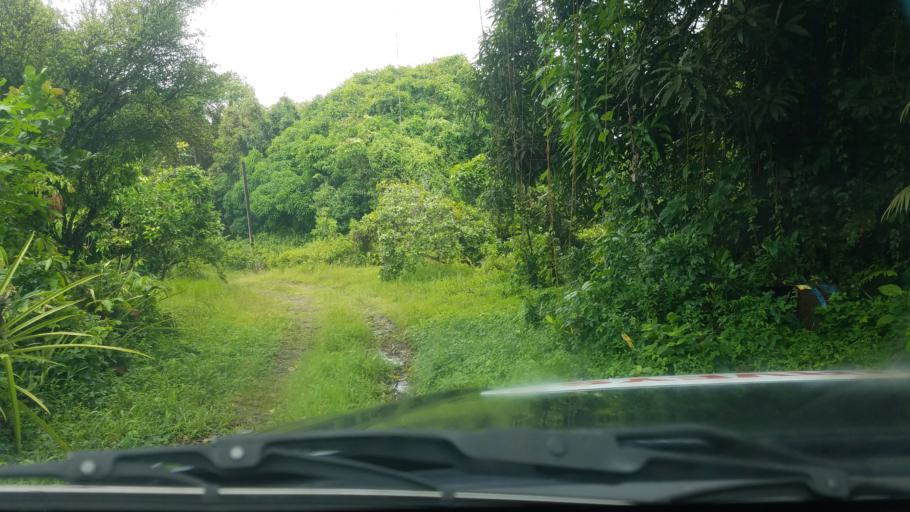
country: LC
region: Castries Quarter
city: Bisee
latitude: 13.9941
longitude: -60.9586
